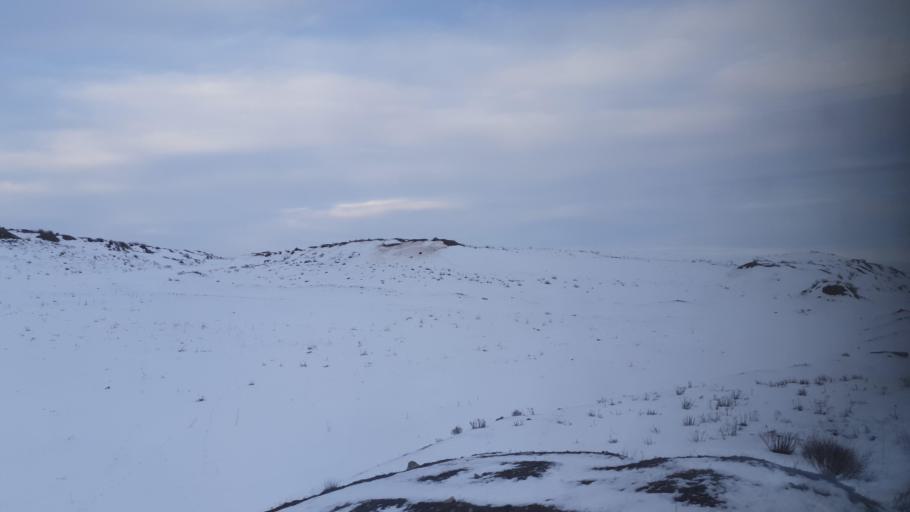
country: TR
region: Yozgat
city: Yerkoy
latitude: 39.6862
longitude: 34.4145
